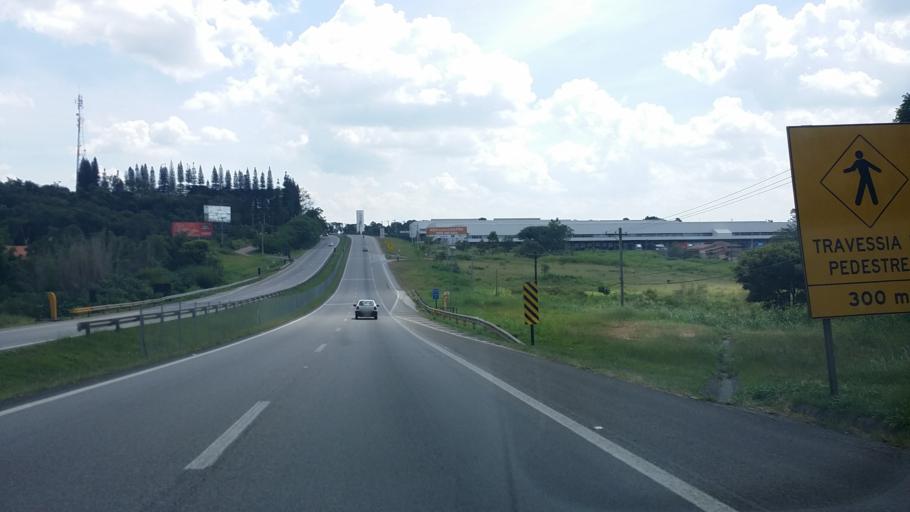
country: BR
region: Sao Paulo
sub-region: Itupeva
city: Itupeva
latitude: -23.2001
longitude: -47.0017
